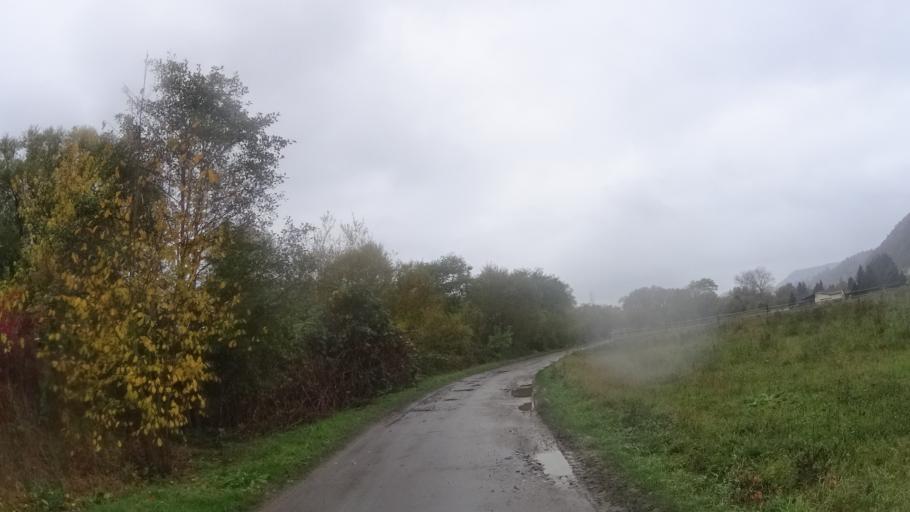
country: DE
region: Thuringia
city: Freienorla
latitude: 50.7740
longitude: 11.5492
